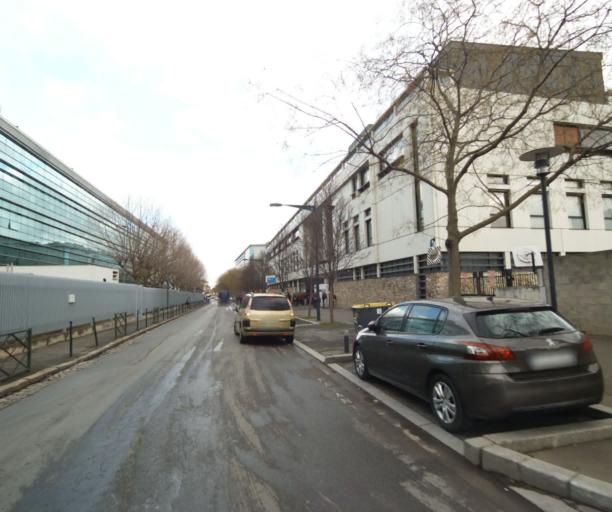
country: FR
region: Ile-de-France
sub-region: Departement des Hauts-de-Seine
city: La Defense
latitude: 48.9015
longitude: 2.2359
